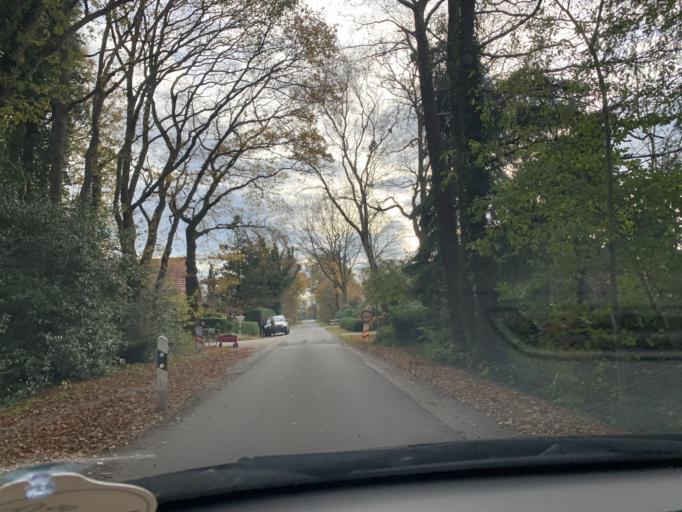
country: DE
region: Lower Saxony
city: Apen
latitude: 53.2210
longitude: 7.7847
